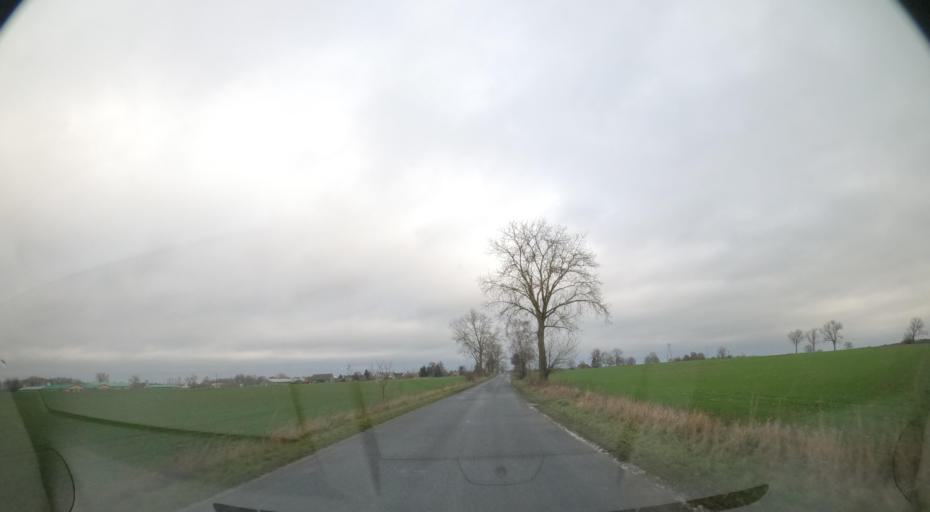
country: PL
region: Greater Poland Voivodeship
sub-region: Powiat pilski
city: Wysoka
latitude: 53.2546
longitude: 17.1509
